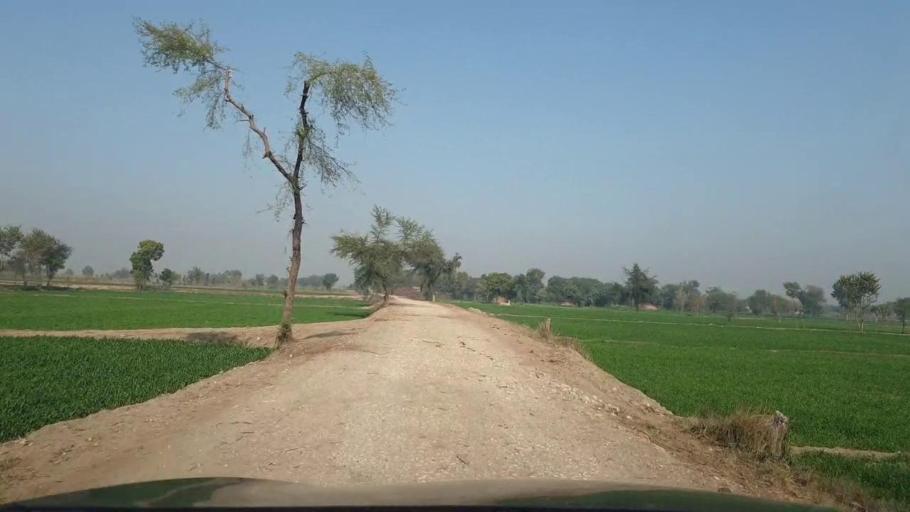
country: PK
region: Sindh
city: Ubauro
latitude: 28.1186
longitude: 69.7510
